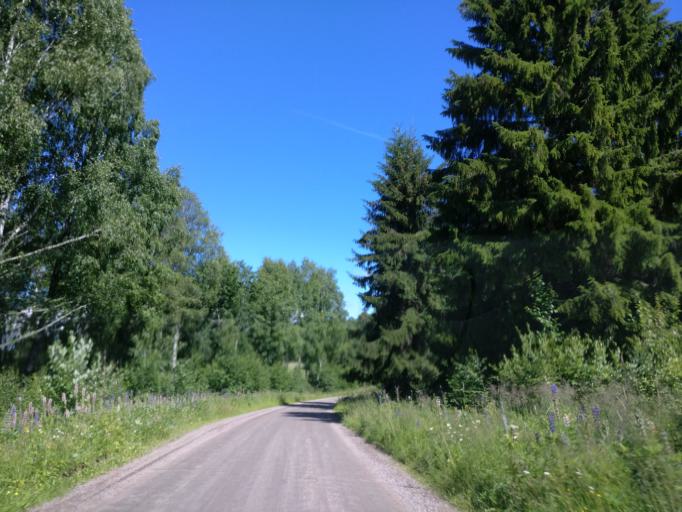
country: SE
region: Vaermland
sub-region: Hagfors Kommun
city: Hagfors
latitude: 60.0401
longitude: 13.6458
